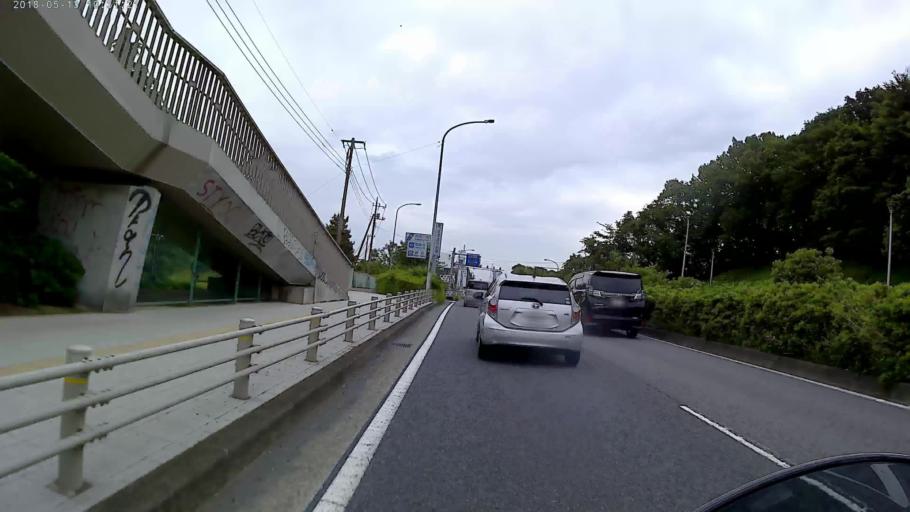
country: JP
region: Tokyo
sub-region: Machida-shi
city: Machida
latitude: 35.5149
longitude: 139.4806
